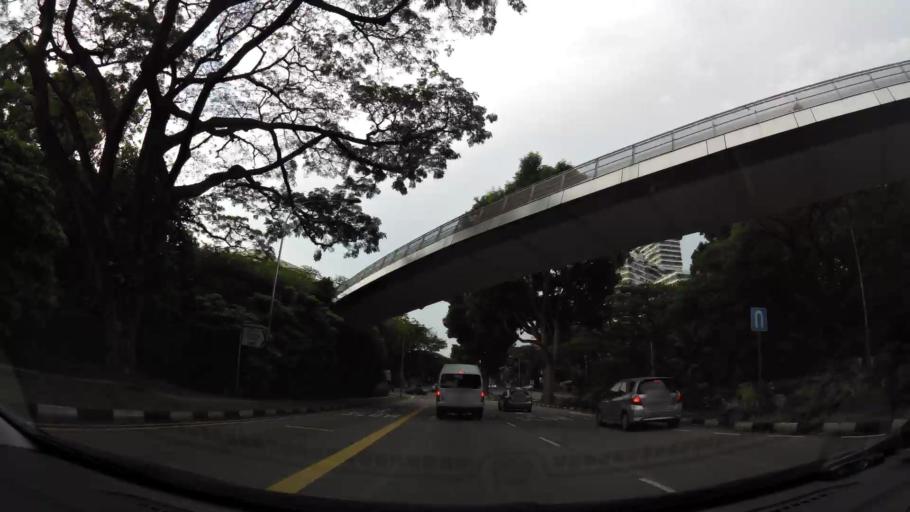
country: SG
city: Singapore
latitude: 1.2800
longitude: 103.8026
